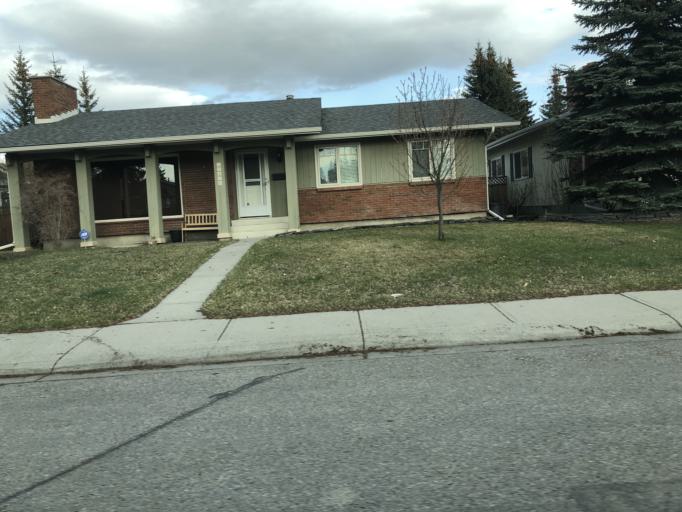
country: CA
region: Alberta
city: Calgary
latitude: 50.9411
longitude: -114.0399
